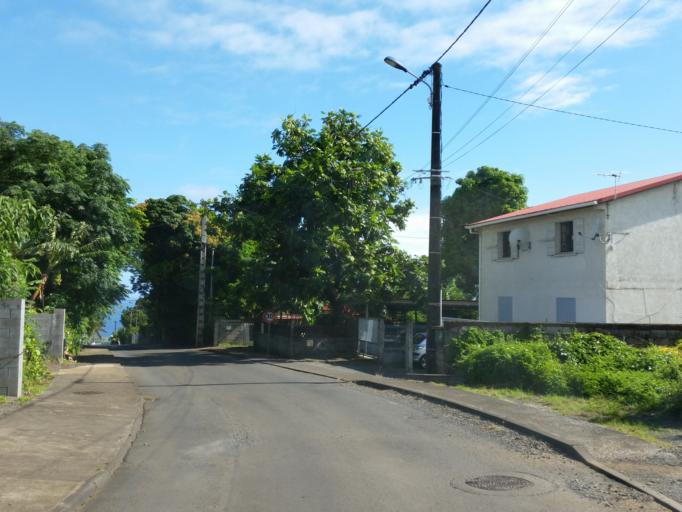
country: RE
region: Reunion
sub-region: Reunion
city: Sainte-Marie
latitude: -20.9202
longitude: 55.5315
